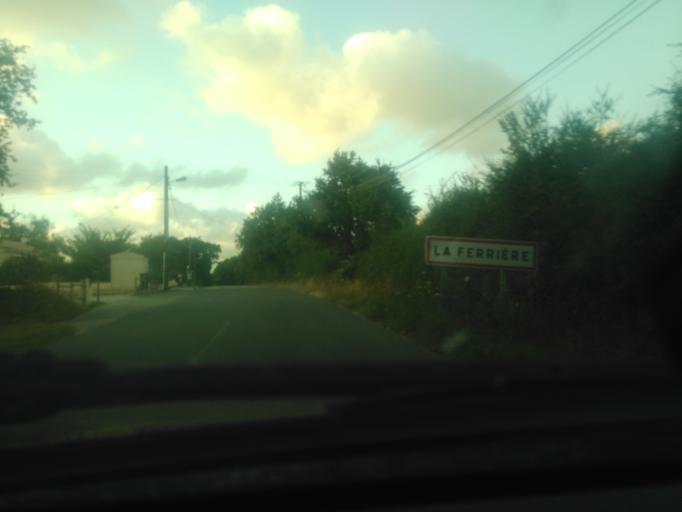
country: FR
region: Pays de la Loire
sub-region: Departement de la Vendee
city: La Ferriere
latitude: 46.7072
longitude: -1.3210
